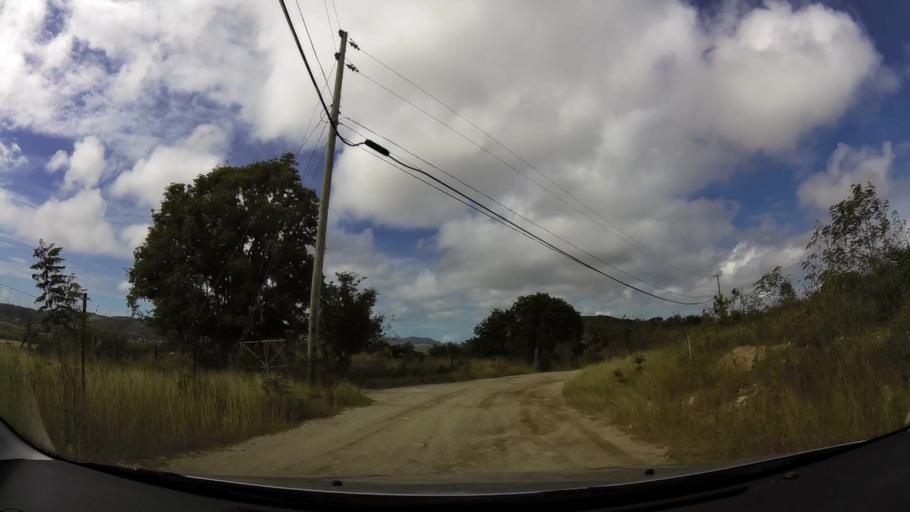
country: AG
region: Saint Paul
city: Liberta
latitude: 17.0553
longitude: -61.7348
